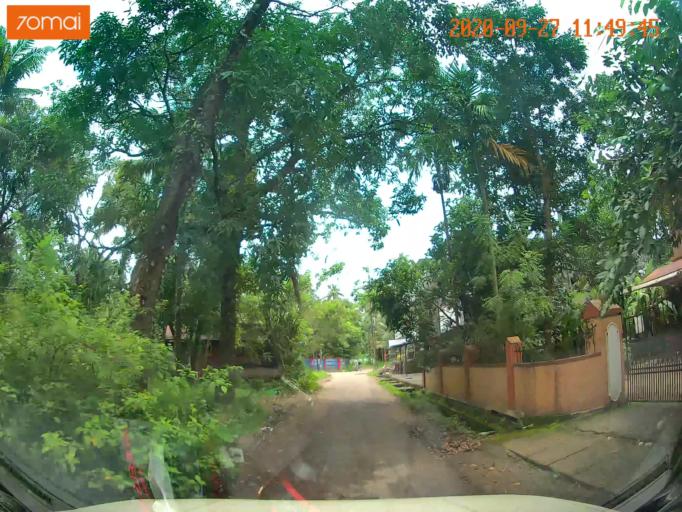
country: IN
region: Kerala
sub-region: Thrissur District
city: Thanniyam
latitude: 10.4715
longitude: 76.1155
